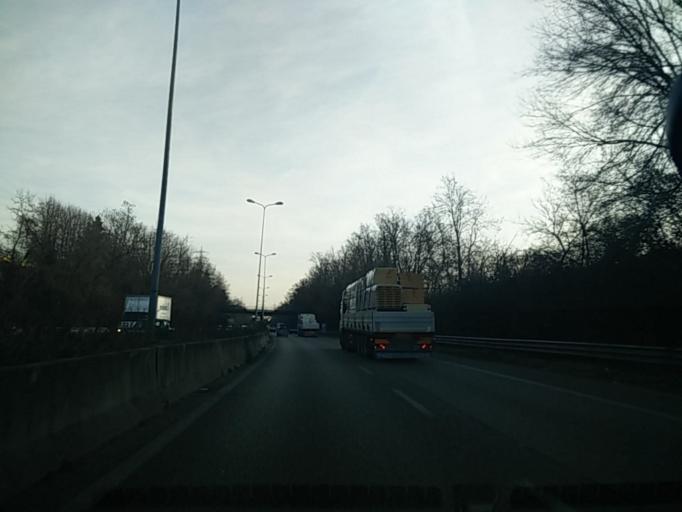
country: IT
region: Lombardy
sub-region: Provincia di Monza e Brianza
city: Varedo
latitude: 45.6079
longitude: 9.1660
